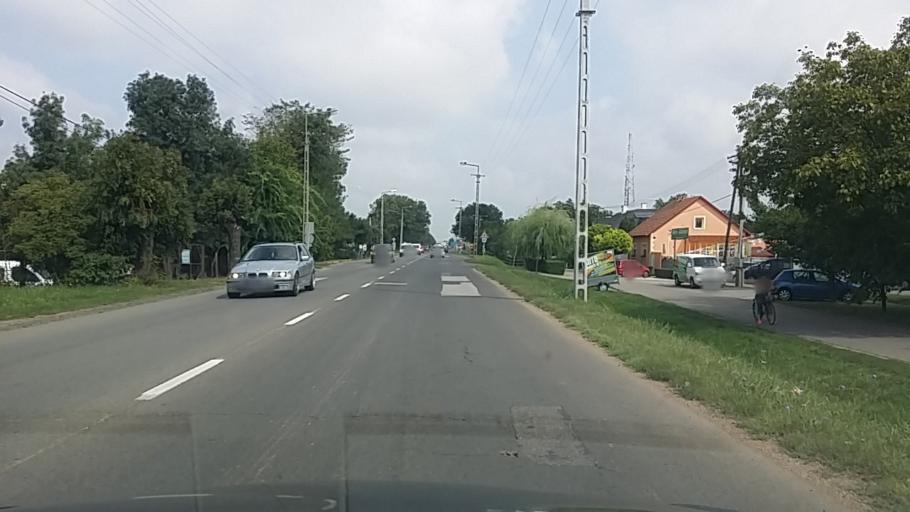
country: HU
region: Csongrad
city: Szeged
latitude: 46.2851
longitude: 20.1712
